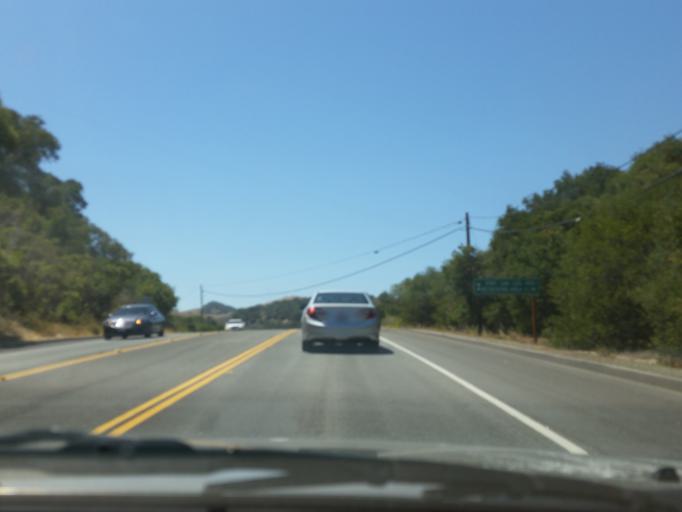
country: US
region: California
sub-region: San Luis Obispo County
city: Avila Beach
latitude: 35.1802
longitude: -120.7258
